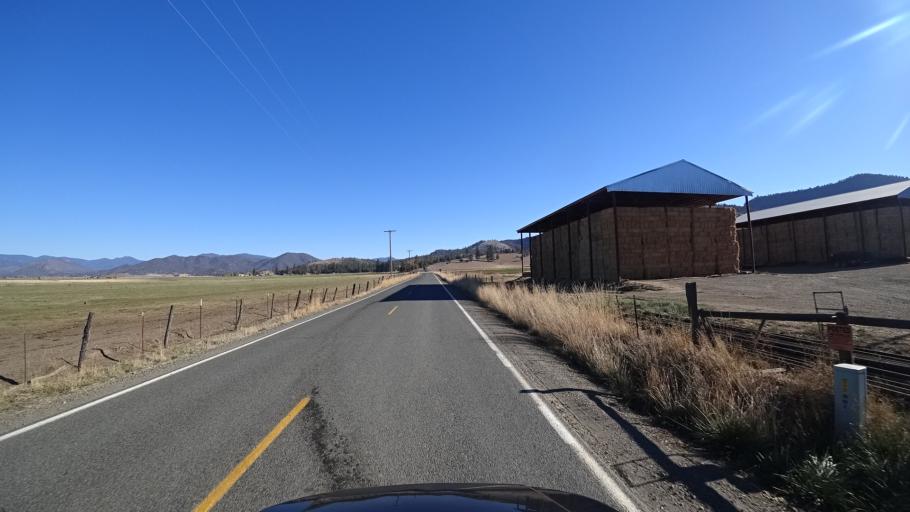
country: US
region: California
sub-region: Siskiyou County
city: Yreka
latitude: 41.5368
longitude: -122.8347
